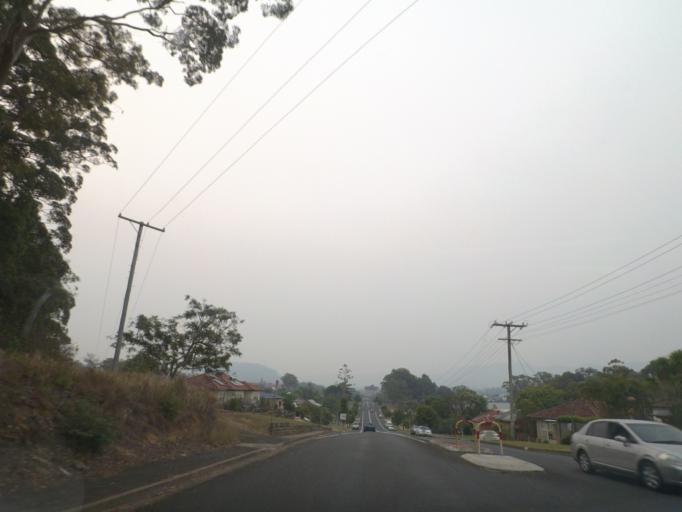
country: AU
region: New South Wales
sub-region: Coffs Harbour
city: Coffs Harbour
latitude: -30.3039
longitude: 153.1203
